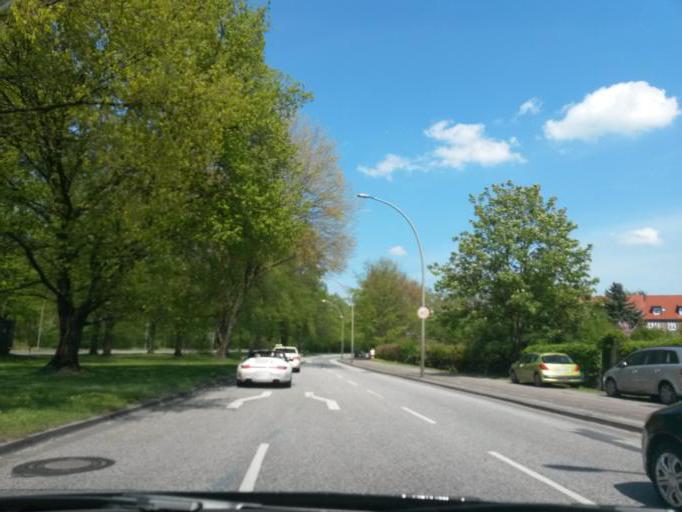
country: DE
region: Hamburg
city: Winterhude
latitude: 53.6036
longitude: 9.9878
